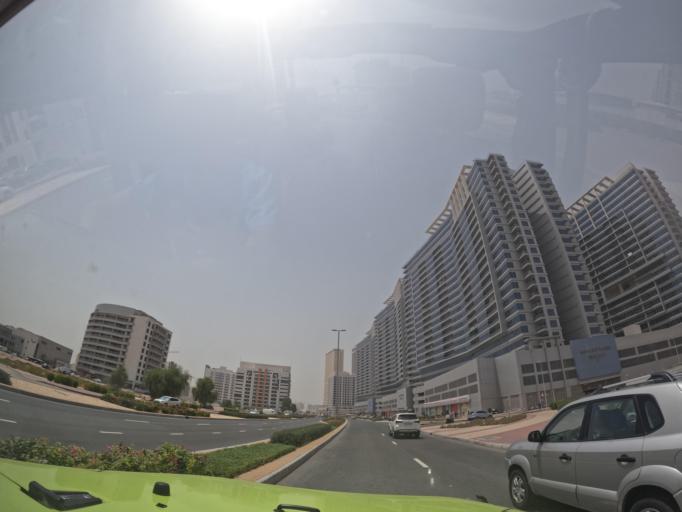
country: AE
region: Dubai
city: Dubai
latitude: 25.0890
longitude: 55.3856
